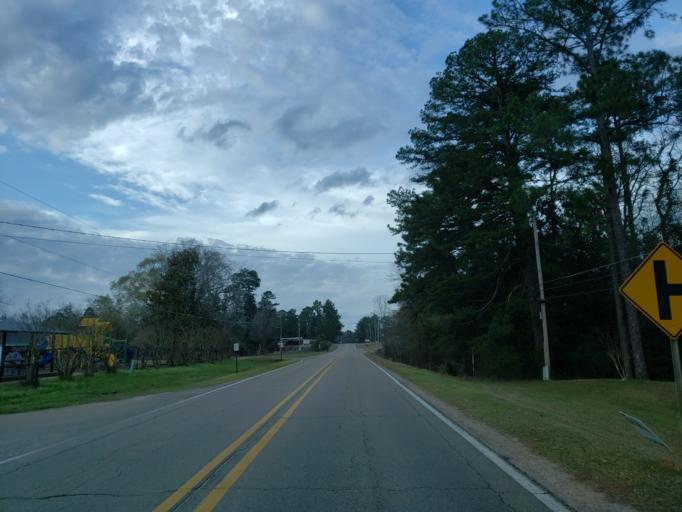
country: US
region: Mississippi
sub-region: Clarke County
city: Stonewall
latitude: 32.2258
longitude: -88.7002
